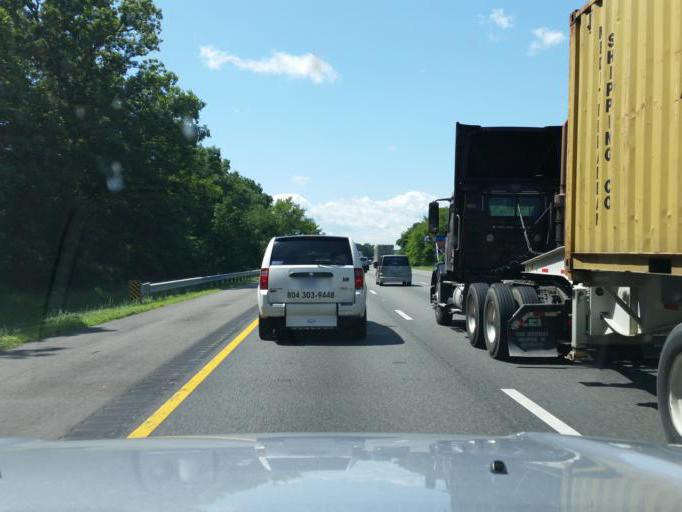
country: US
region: Virginia
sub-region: Hanover County
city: Ashland
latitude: 37.7874
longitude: -77.4600
